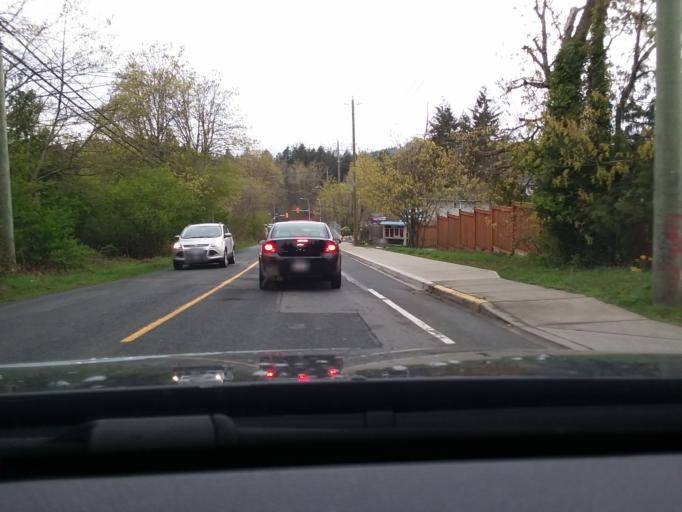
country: CA
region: British Columbia
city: Victoria
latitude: 48.5143
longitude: -123.3817
